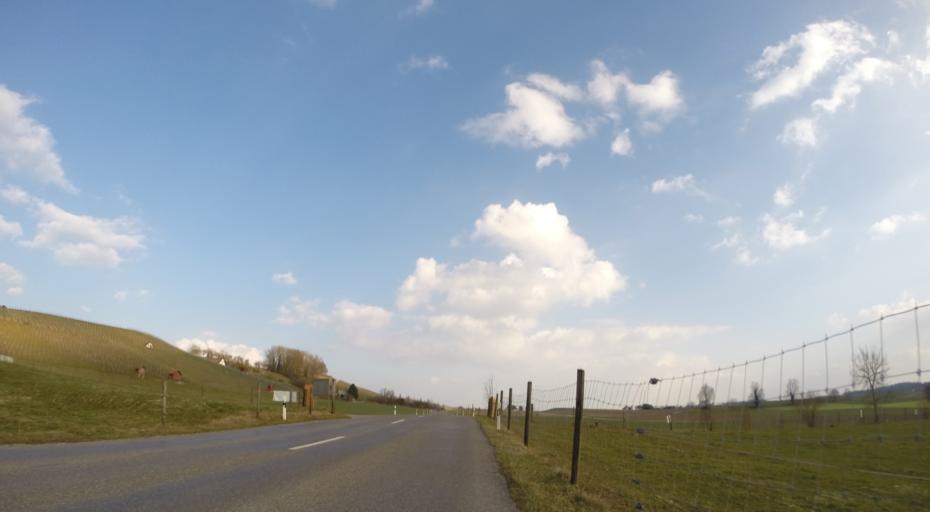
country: CH
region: Thurgau
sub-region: Frauenfeld District
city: Wagenhausen
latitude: 47.6304
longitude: 8.8043
